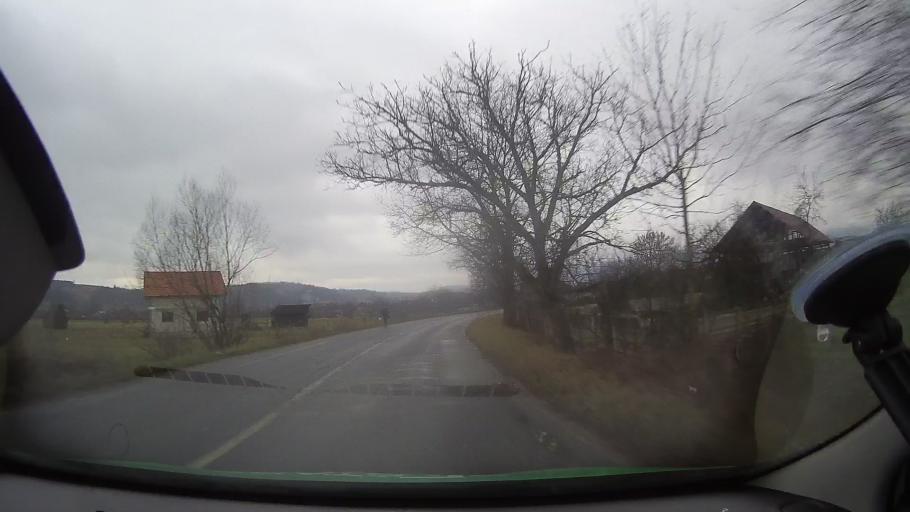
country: RO
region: Arad
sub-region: Comuna Halmagiu
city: Halmagiu
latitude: 46.2662
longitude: 22.5972
